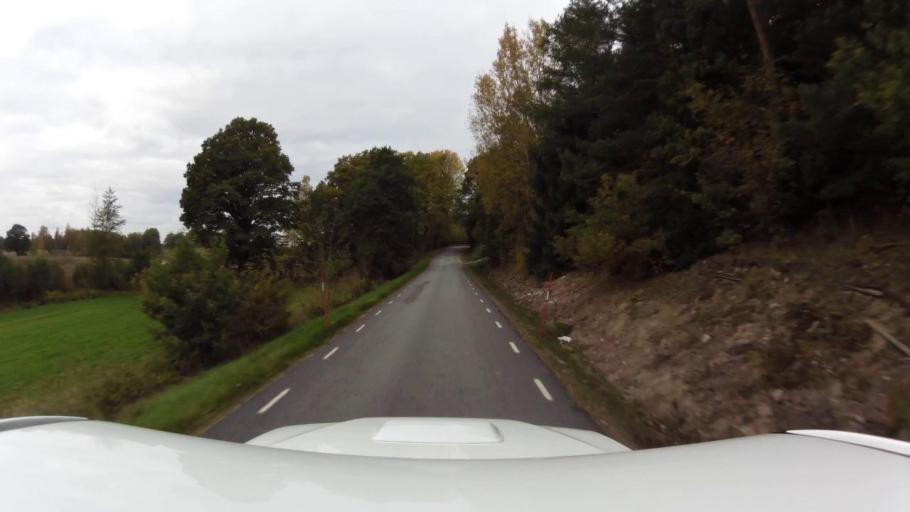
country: SE
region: OEstergoetland
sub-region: Linkopings Kommun
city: Ljungsbro
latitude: 58.5394
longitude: 15.4182
